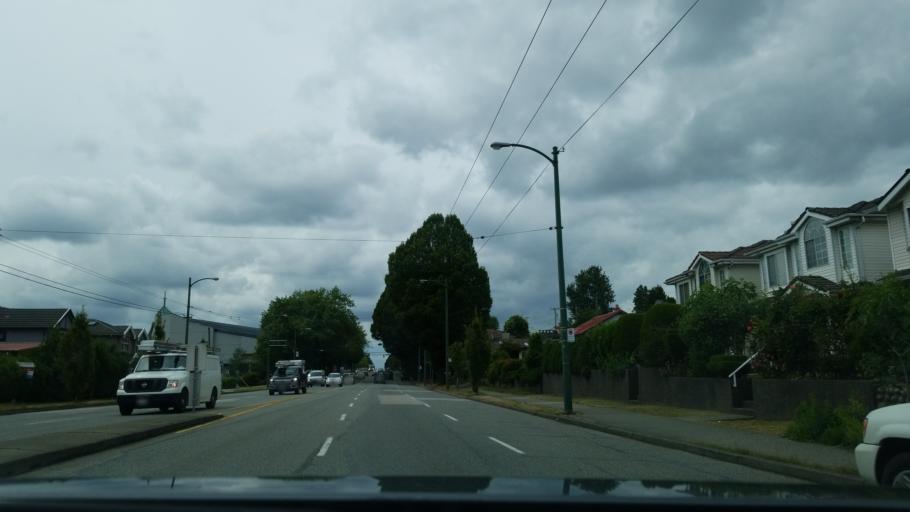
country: CA
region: British Columbia
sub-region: Fraser Valley Regional District
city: North Vancouver
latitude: 49.2620
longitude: -123.0456
